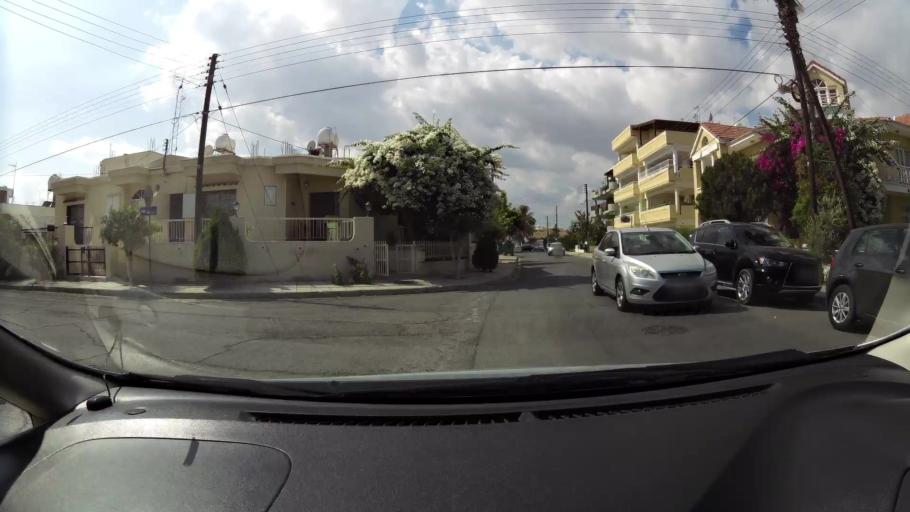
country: CY
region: Larnaka
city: Larnaca
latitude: 34.9201
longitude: 33.6043
